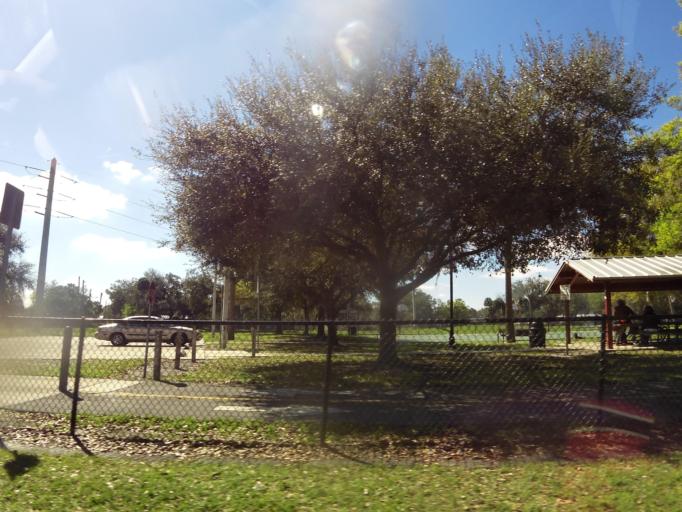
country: US
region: Florida
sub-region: Seminole County
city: Sanford
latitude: 28.8045
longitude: -81.2764
